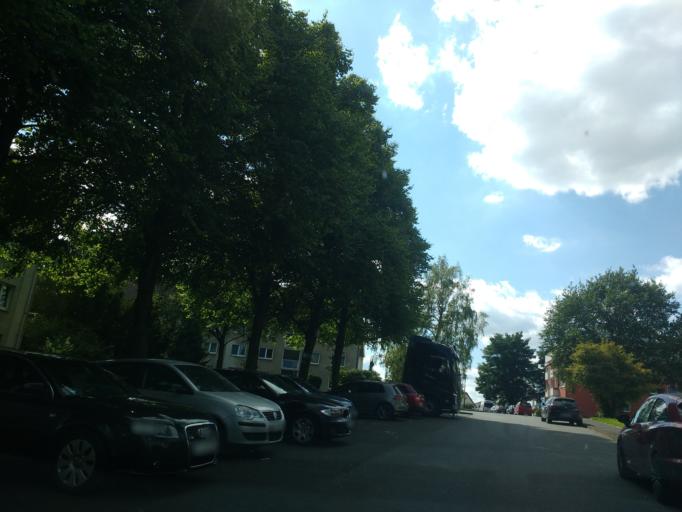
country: DE
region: North Rhine-Westphalia
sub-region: Regierungsbezirk Detmold
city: Lemgo
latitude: 52.0332
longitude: 8.8894
